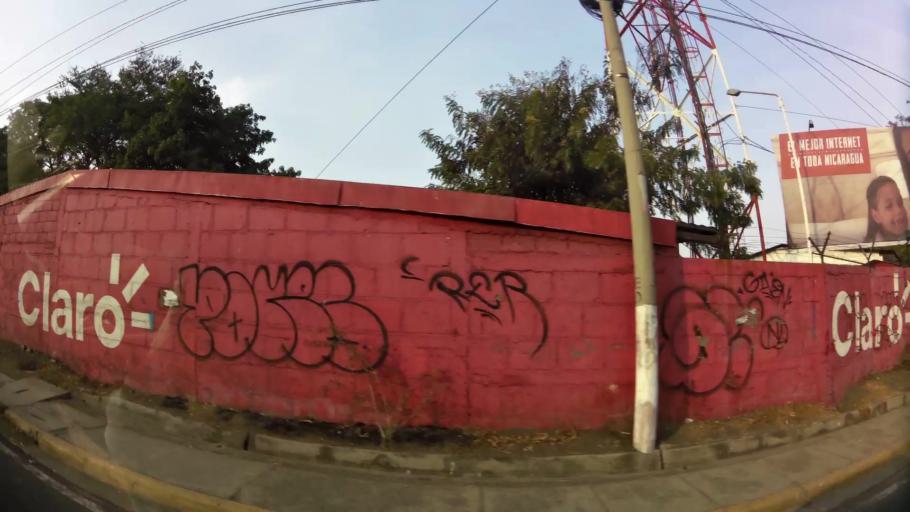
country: NI
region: Managua
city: Ciudad Sandino
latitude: 12.1303
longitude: -86.3117
